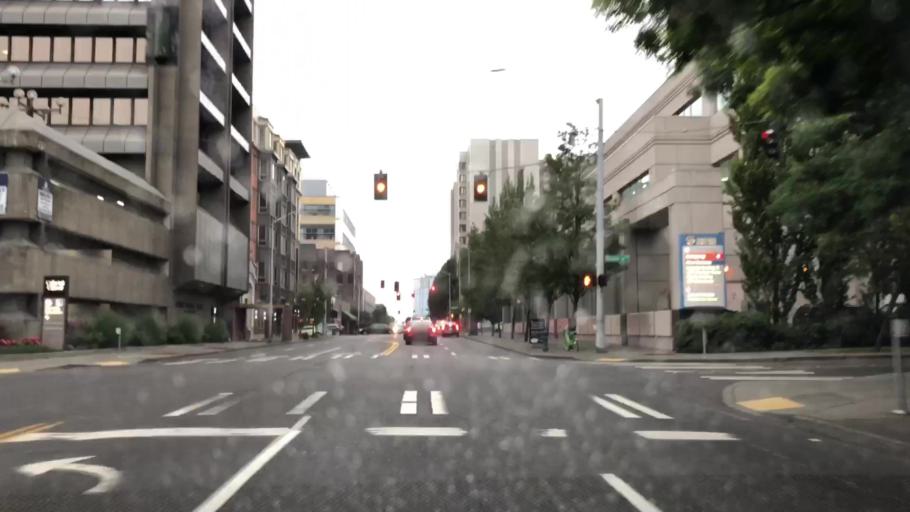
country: US
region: Washington
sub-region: Kitsap County
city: Manchester
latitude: 47.5773
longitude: -122.4962
